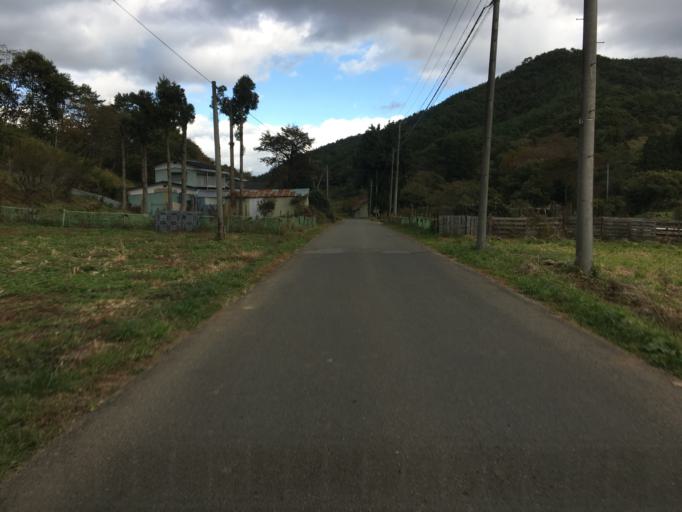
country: JP
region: Fukushima
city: Yanagawamachi-saiwaicho
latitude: 37.7804
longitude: 140.7150
